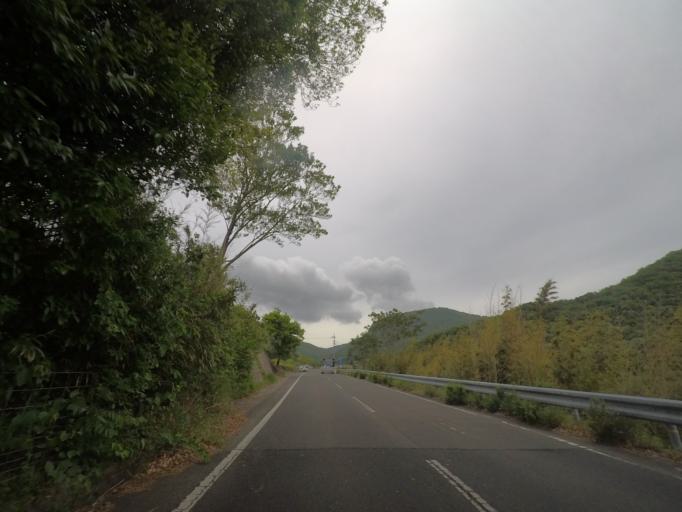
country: JP
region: Kagawa
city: Tonosho
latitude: 34.5027
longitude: 134.2374
